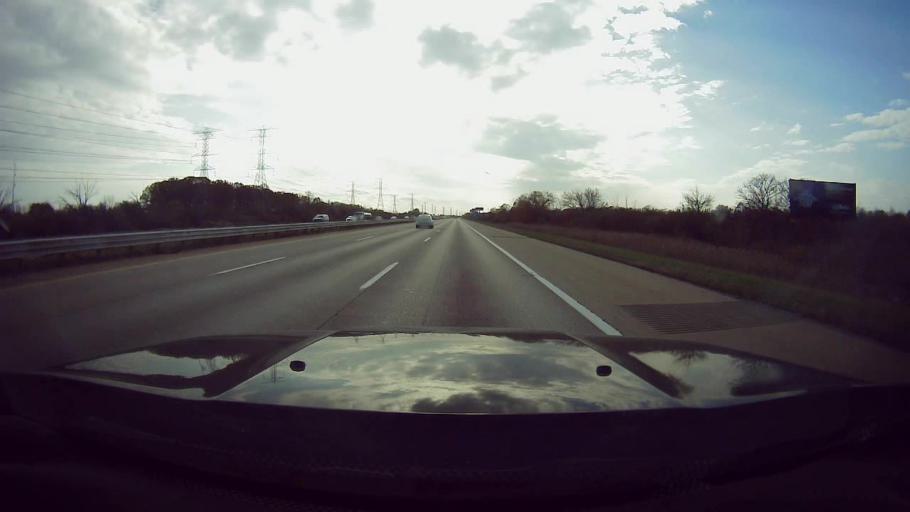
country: US
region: Michigan
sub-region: Monroe County
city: South Rockwood
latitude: 42.0199
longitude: -83.3016
